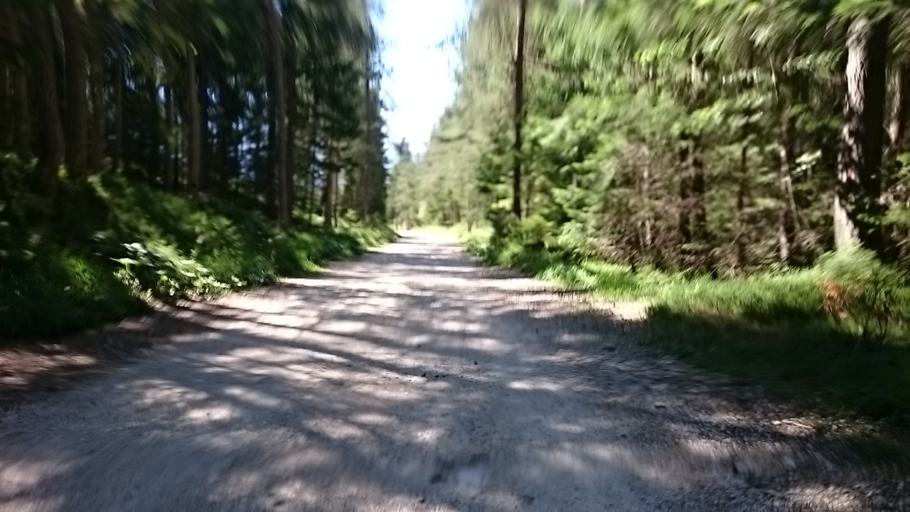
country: IT
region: Veneto
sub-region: Provincia di Belluno
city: Cortina d'Ampezzo
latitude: 46.5666
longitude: 12.1239
